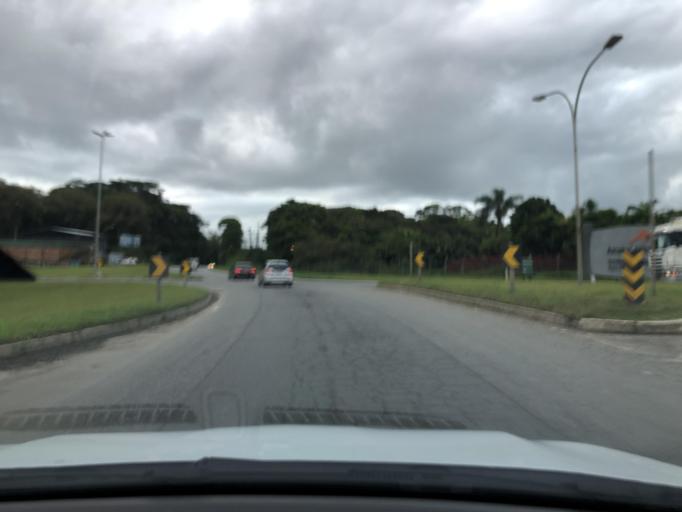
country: BR
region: Santa Catarina
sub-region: Sao Francisco Do Sul
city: Sao Francisco do Sul
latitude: -26.2957
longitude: -48.6424
